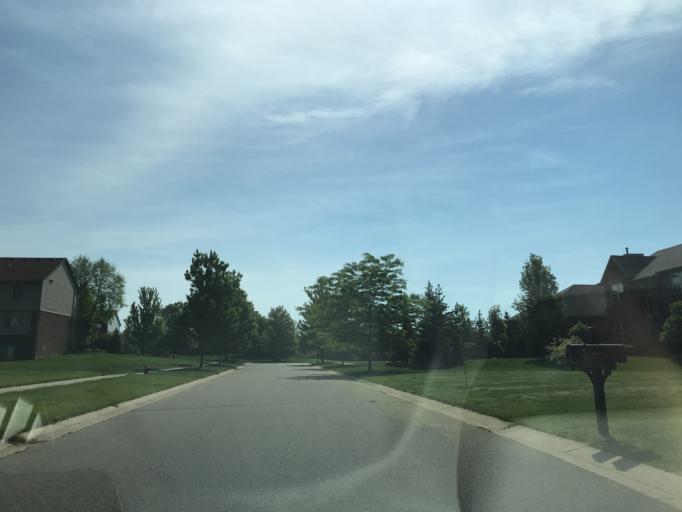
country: US
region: Michigan
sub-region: Oakland County
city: South Lyon
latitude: 42.4766
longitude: -83.6357
